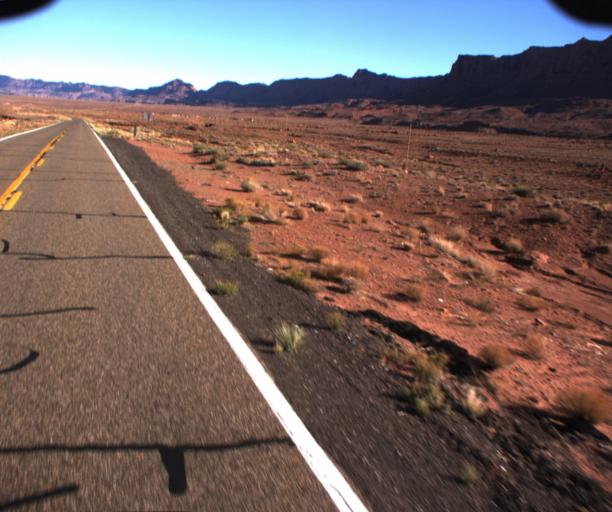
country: US
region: Arizona
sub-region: Coconino County
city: LeChee
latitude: 36.7291
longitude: -111.6403
